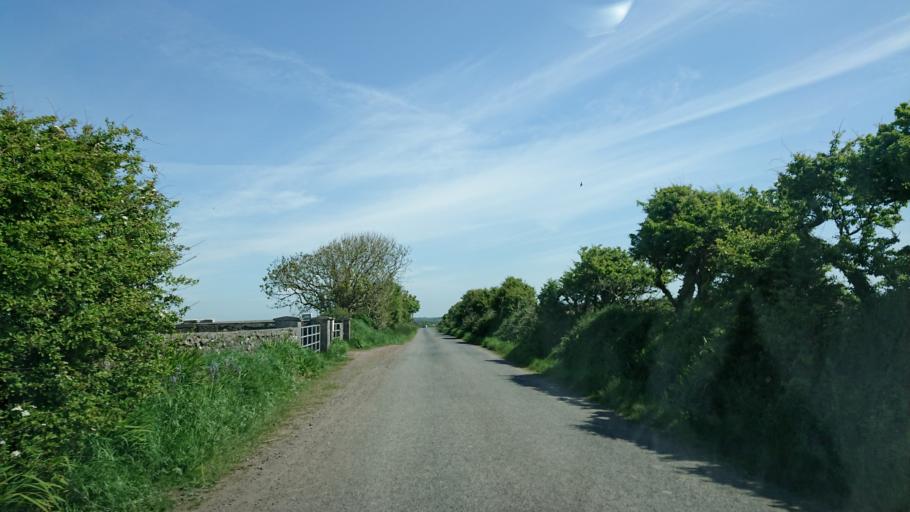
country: IE
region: Munster
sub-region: Waterford
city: Tra Mhor
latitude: 52.1461
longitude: -7.0818
